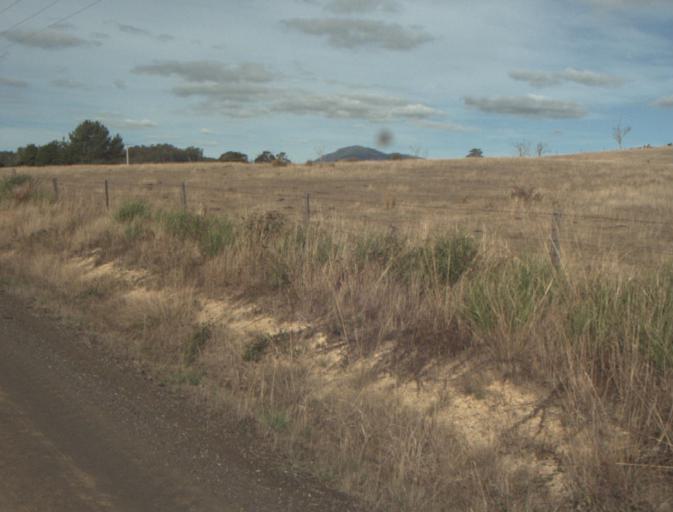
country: AU
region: Tasmania
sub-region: Launceston
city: Mayfield
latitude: -41.2198
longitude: 147.1541
